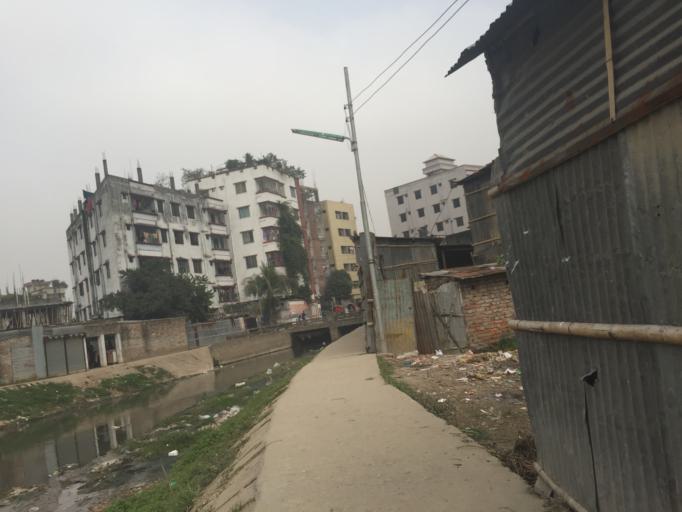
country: BD
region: Dhaka
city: Azimpur
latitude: 23.7822
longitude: 90.3655
